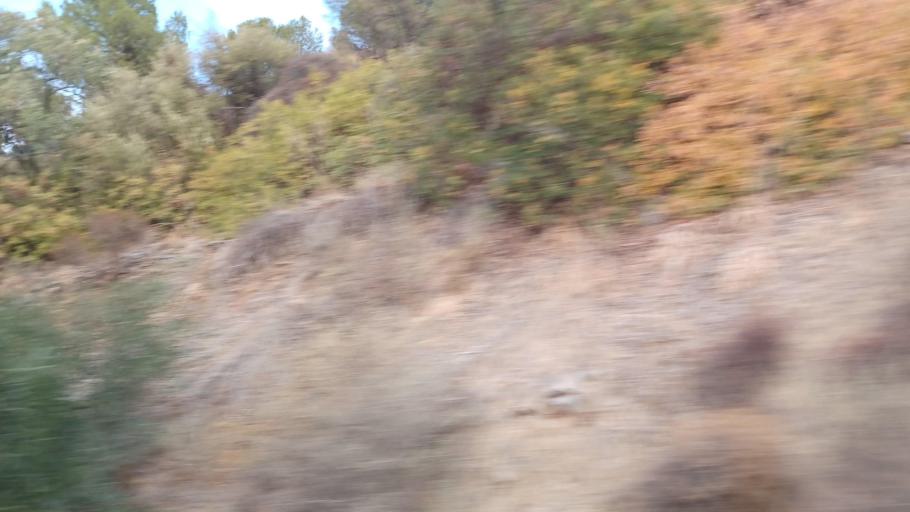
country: CY
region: Lefkosia
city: Kakopetria
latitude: 35.0027
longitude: 32.8978
